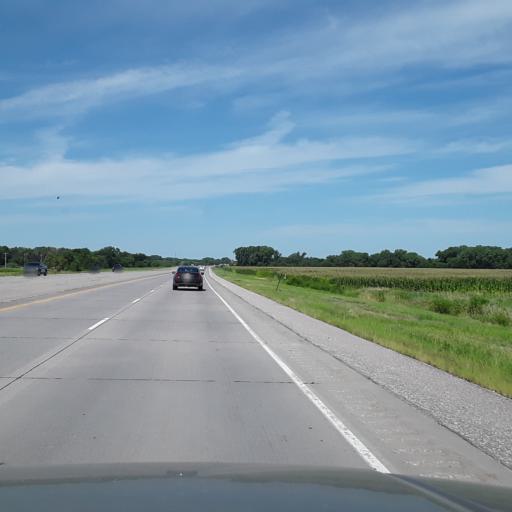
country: US
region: Nebraska
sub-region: Lancaster County
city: Lincoln
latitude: 40.8796
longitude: -96.7667
